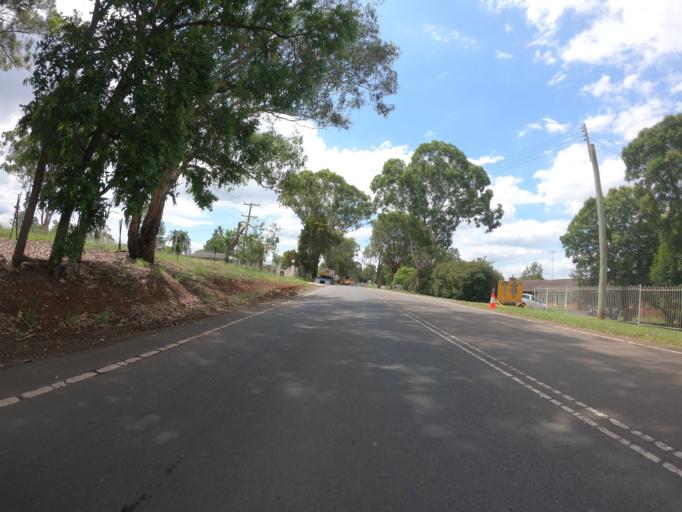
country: AU
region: New South Wales
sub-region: Penrith Municipality
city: Kingswood Park
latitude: -33.8208
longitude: 150.7607
